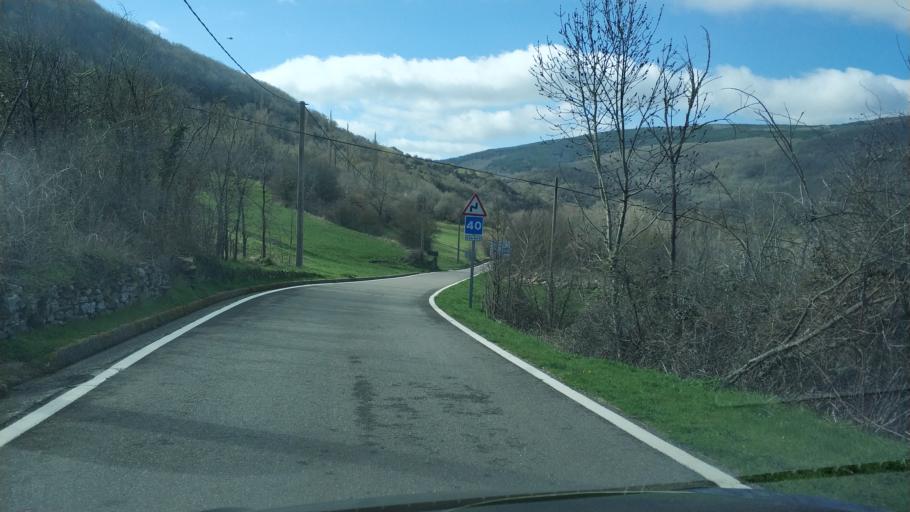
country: ES
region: Castille and Leon
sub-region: Provincia de Burgos
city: Arija
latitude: 42.9048
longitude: -4.0316
